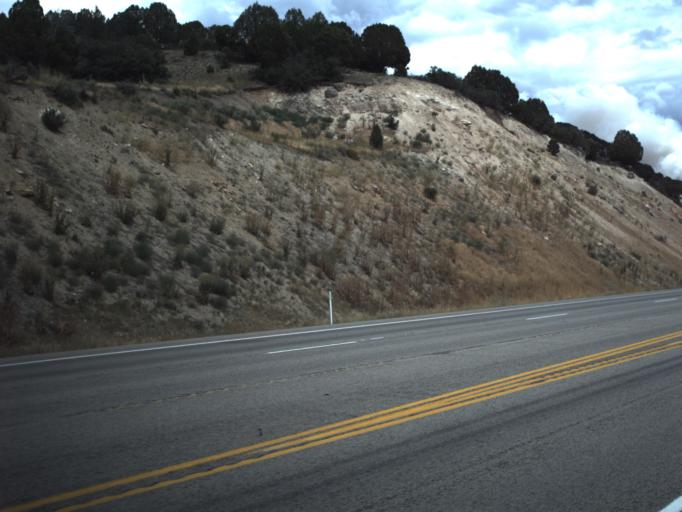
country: US
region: Utah
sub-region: Utah County
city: Mapleton
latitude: 39.9952
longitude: -111.4664
